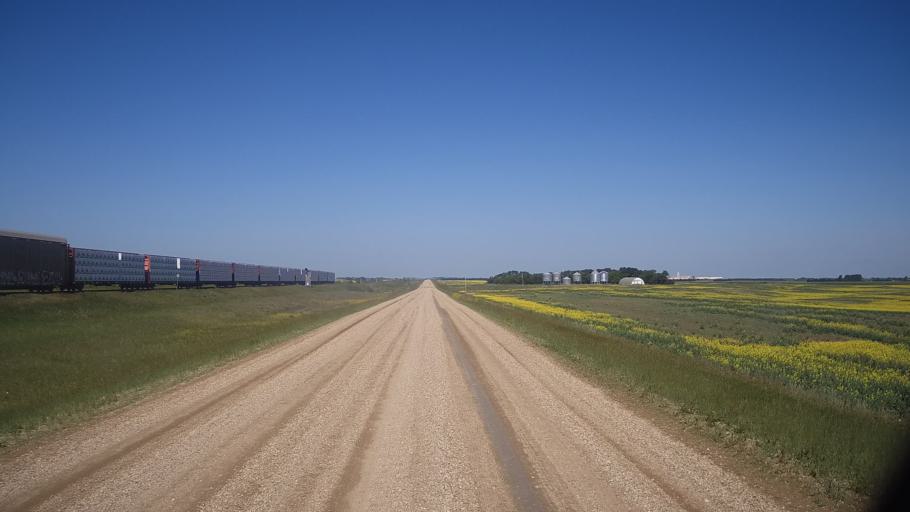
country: CA
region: Saskatchewan
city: Watrous
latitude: 51.8611
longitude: -105.9649
